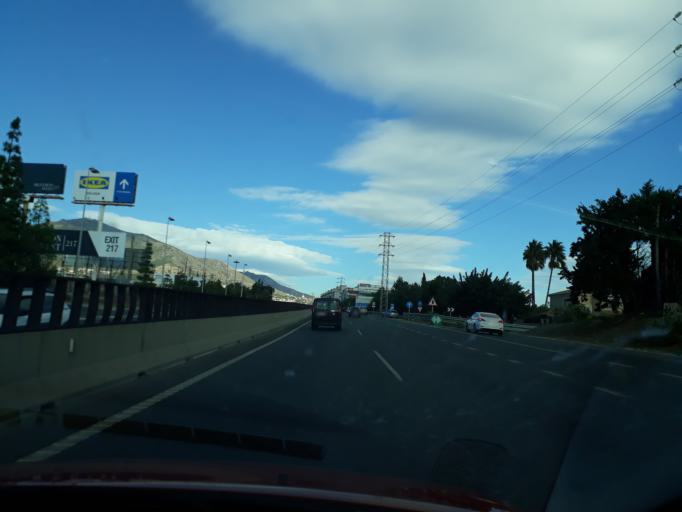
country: ES
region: Andalusia
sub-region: Provincia de Malaga
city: Fuengirola
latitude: 36.5533
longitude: -4.6235
